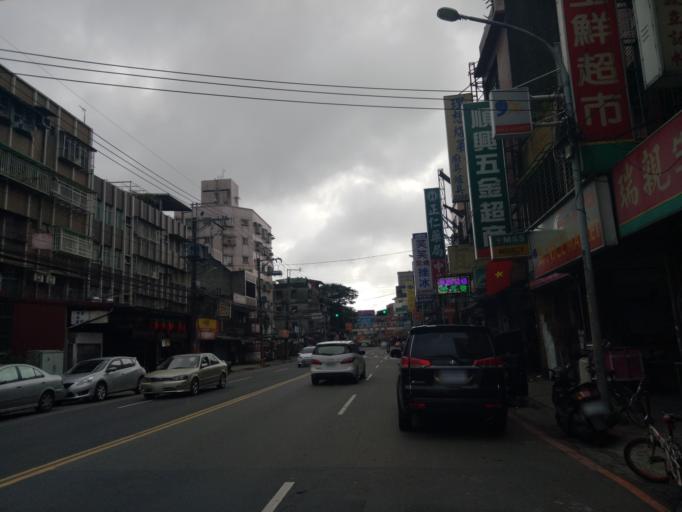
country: TW
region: Taipei
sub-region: Taipei
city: Banqiao
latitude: 24.9572
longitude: 121.4156
